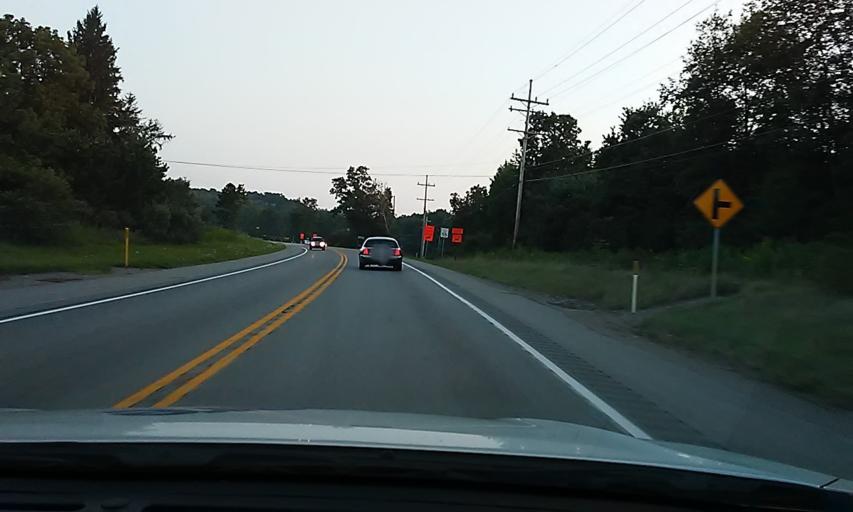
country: US
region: Pennsylvania
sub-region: Clarion County
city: Marianne
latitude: 41.2221
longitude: -79.4353
